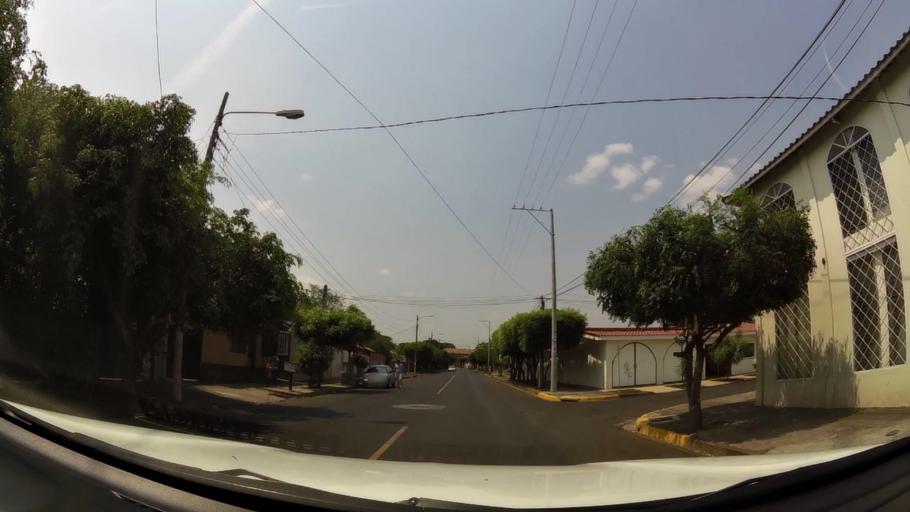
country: NI
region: Managua
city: Ciudad Sandino
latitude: 12.1533
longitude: -86.3124
